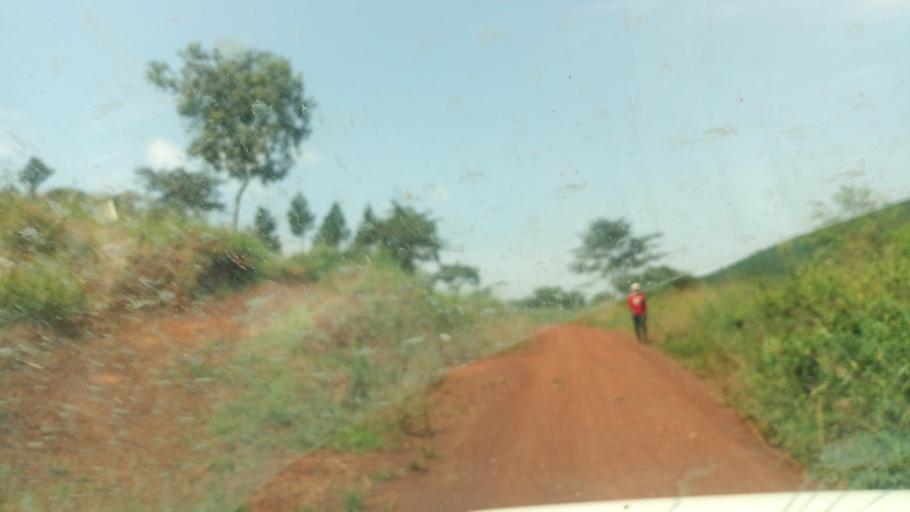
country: UG
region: Western Region
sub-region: Masindi District
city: Masindi
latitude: 1.6484
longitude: 31.8061
